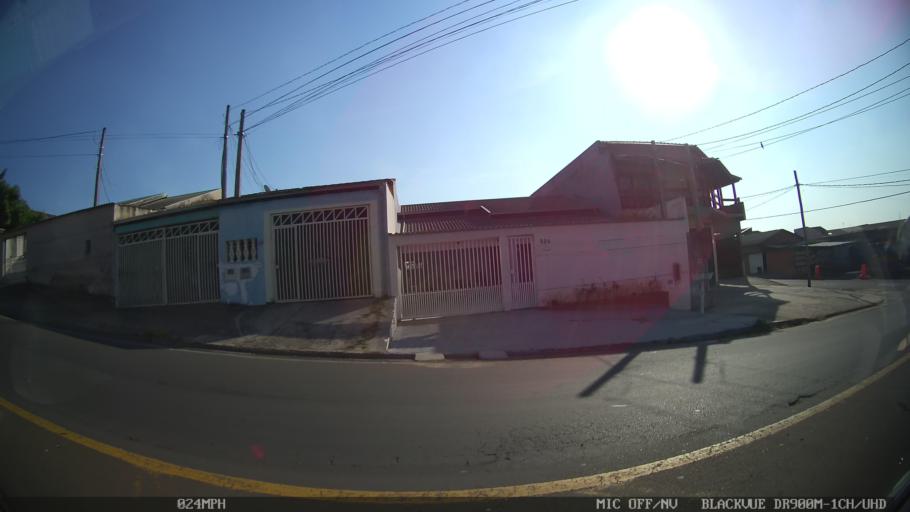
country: BR
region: Sao Paulo
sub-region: Campinas
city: Campinas
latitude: -22.9844
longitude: -47.1411
